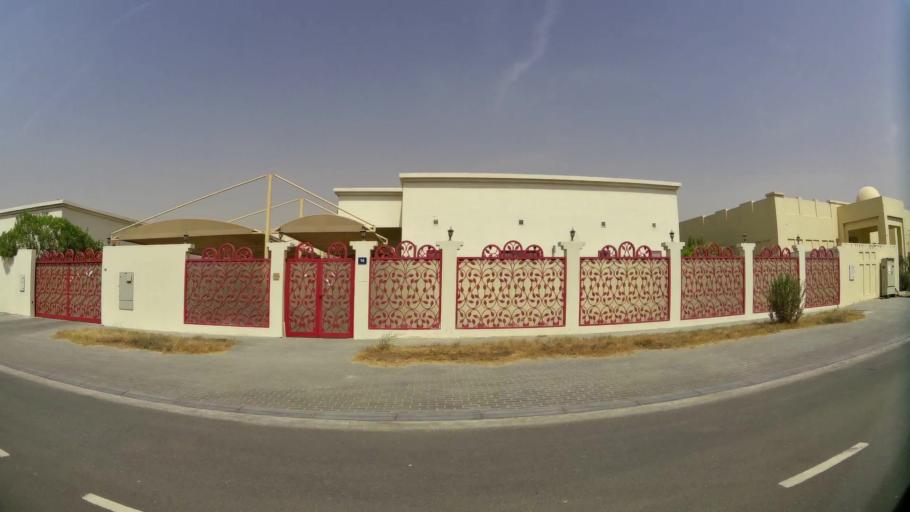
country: AE
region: Ash Shariqah
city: Sharjah
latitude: 25.2571
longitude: 55.4778
